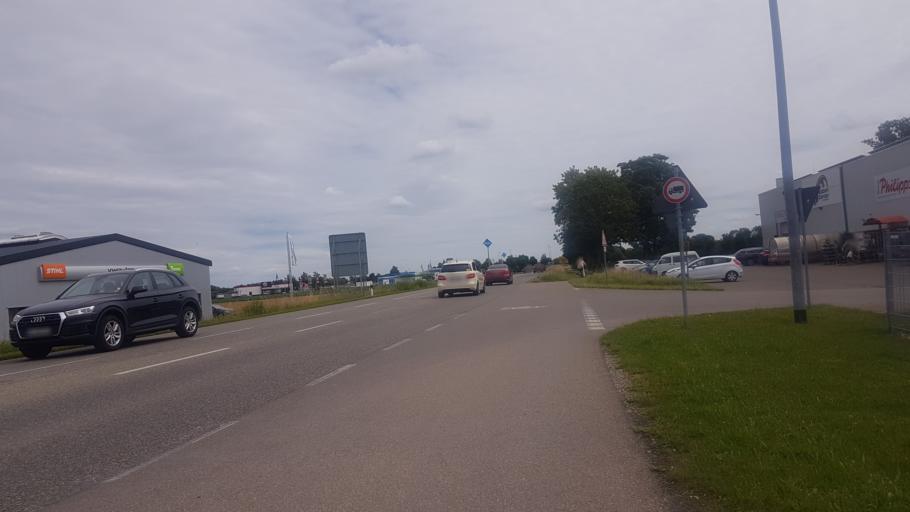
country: DE
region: Bavaria
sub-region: Swabia
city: Lauingen
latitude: 48.5745
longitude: 10.4506
